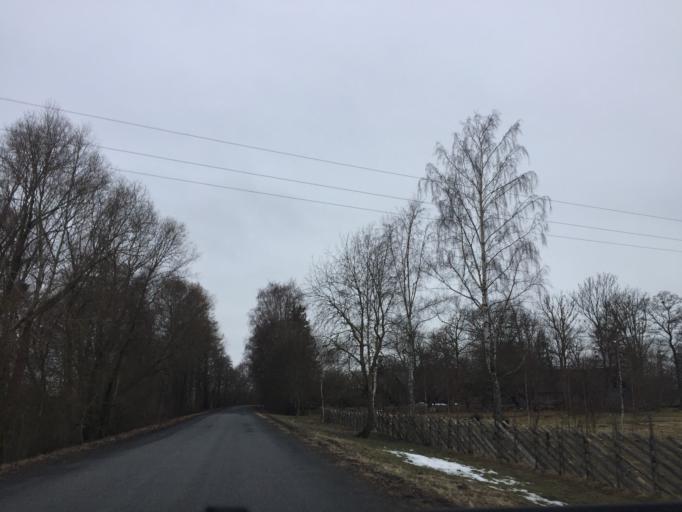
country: EE
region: Laeaene
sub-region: Haapsalu linn
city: Haapsalu
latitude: 58.7825
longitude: 23.4751
